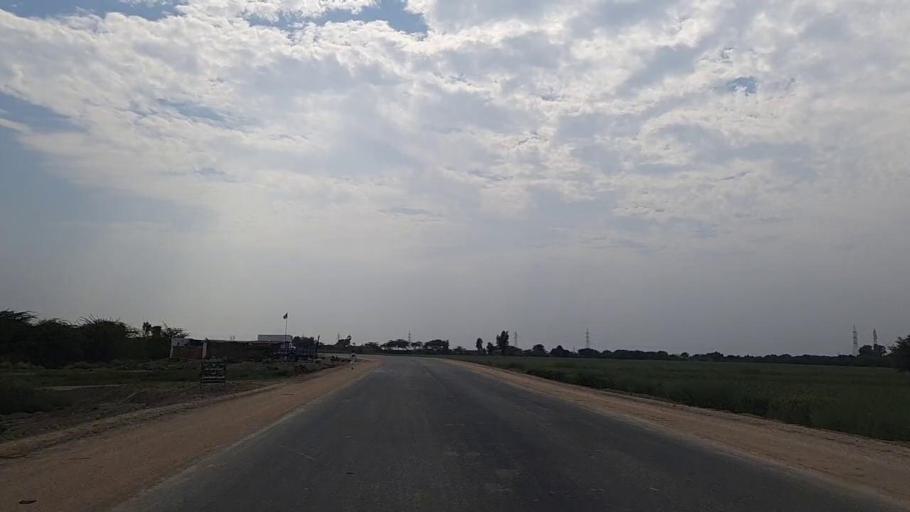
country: PK
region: Sindh
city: Naukot
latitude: 24.9703
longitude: 69.2834
